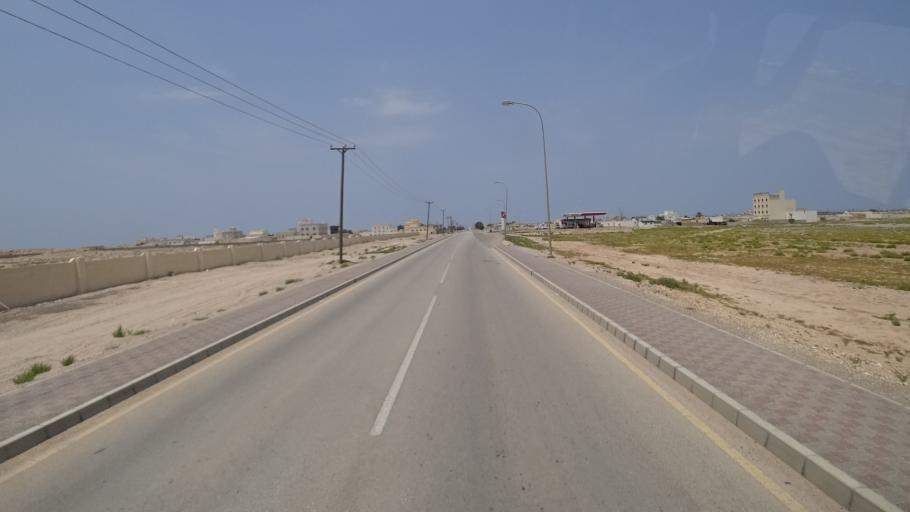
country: OM
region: Ash Sharqiyah
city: Sur
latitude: 22.5117
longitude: 59.7940
